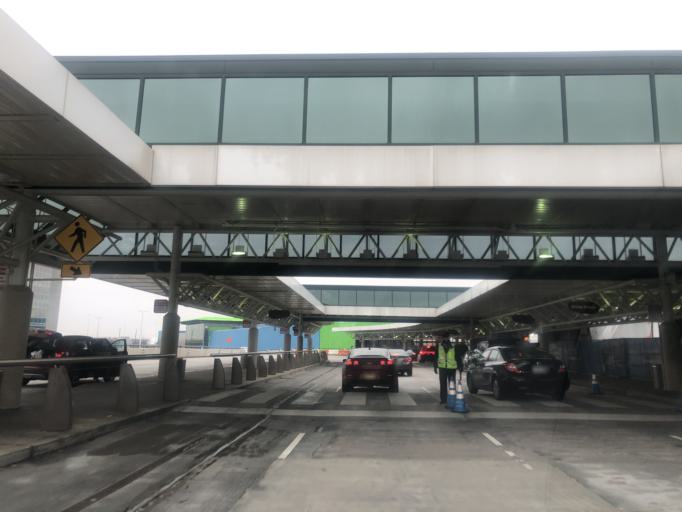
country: US
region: Tennessee
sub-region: Davidson County
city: Lakewood
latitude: 36.1316
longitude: -86.6687
